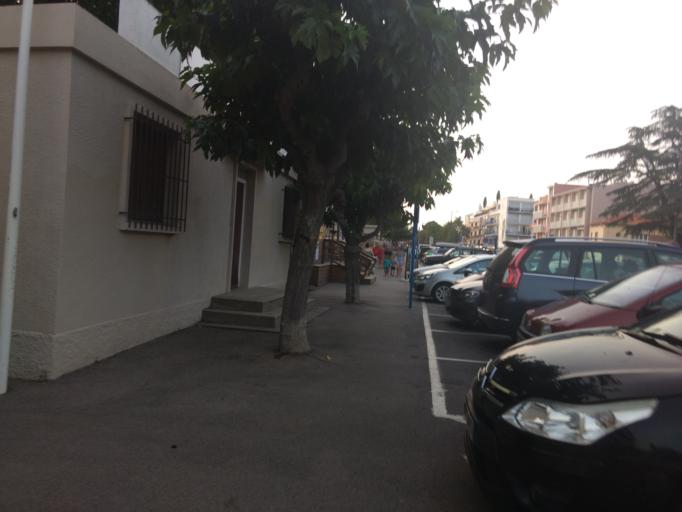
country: FR
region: Languedoc-Roussillon
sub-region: Departement des Pyrenees-Orientales
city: Argelers
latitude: 42.5499
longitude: 3.0467
